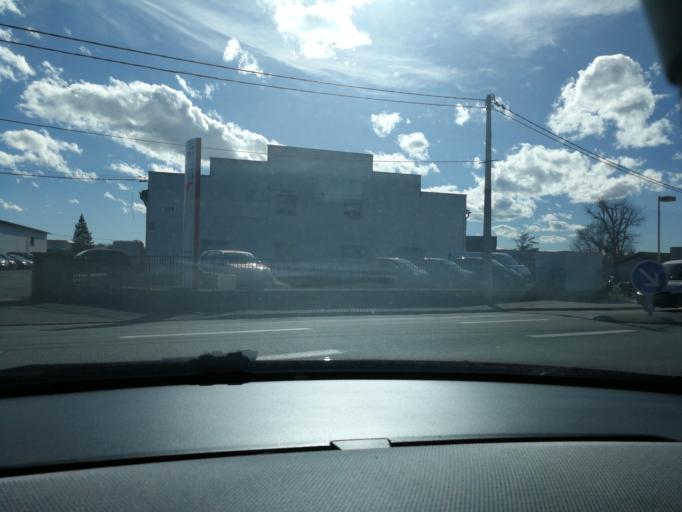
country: FR
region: Midi-Pyrenees
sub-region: Departement de la Haute-Garonne
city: Cugnaux
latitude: 43.5609
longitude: 1.3477
